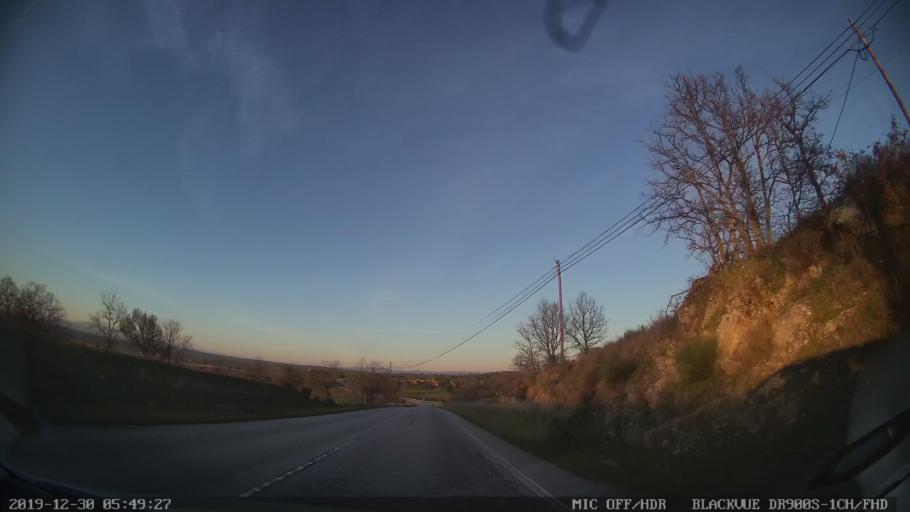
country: PT
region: Castelo Branco
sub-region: Idanha-A-Nova
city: Idanha-a-Nova
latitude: 39.9743
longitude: -7.2422
